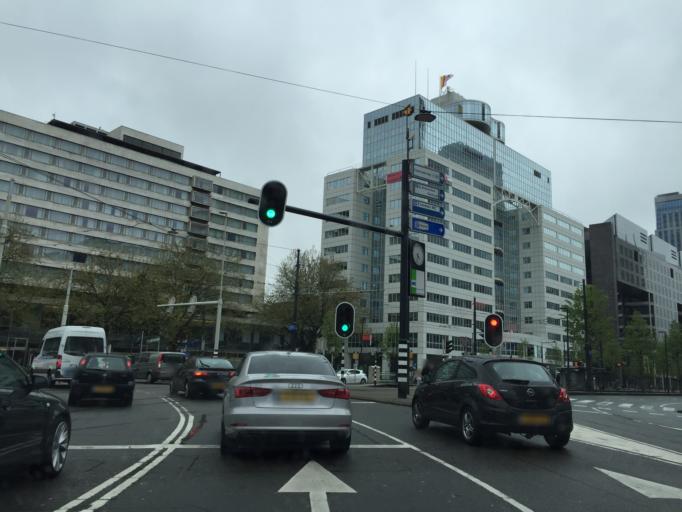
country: NL
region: South Holland
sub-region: Gemeente Rotterdam
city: Rotterdam
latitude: 51.9246
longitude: 4.4772
